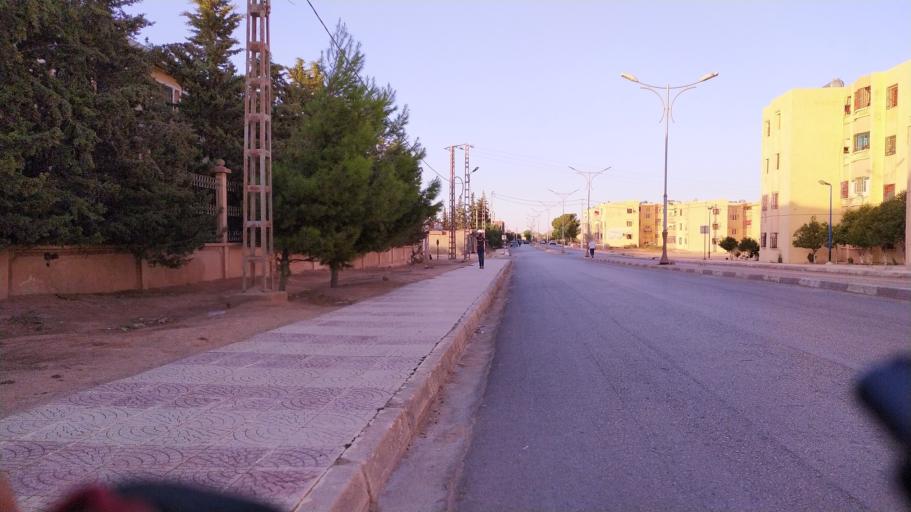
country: DZ
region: Tiaret
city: Frenda
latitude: 34.8883
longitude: 1.2416
